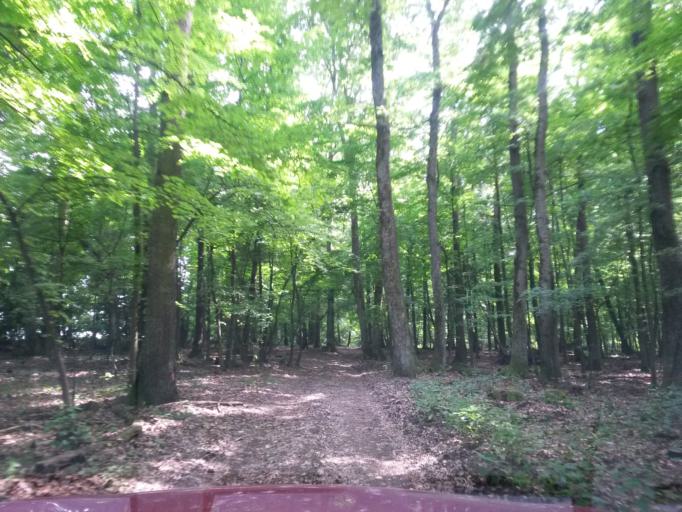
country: SK
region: Kosicky
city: Moldava nad Bodvou
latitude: 48.6373
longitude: 21.1034
